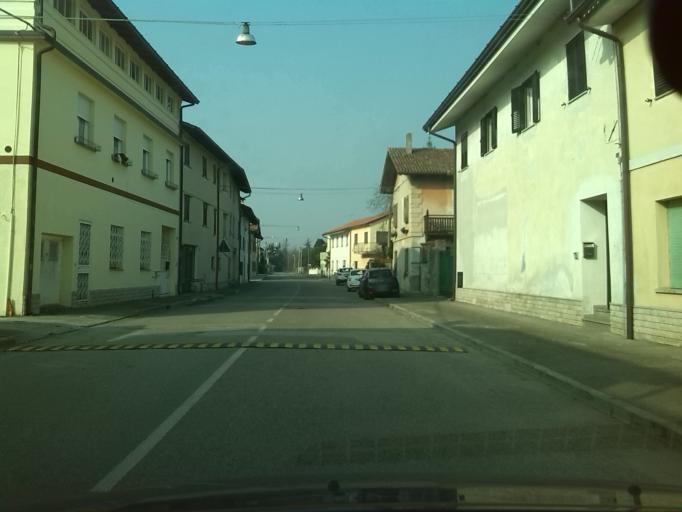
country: IT
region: Friuli Venezia Giulia
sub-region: Provincia di Gorizia
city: Moraro
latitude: 45.9223
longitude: 13.4819
